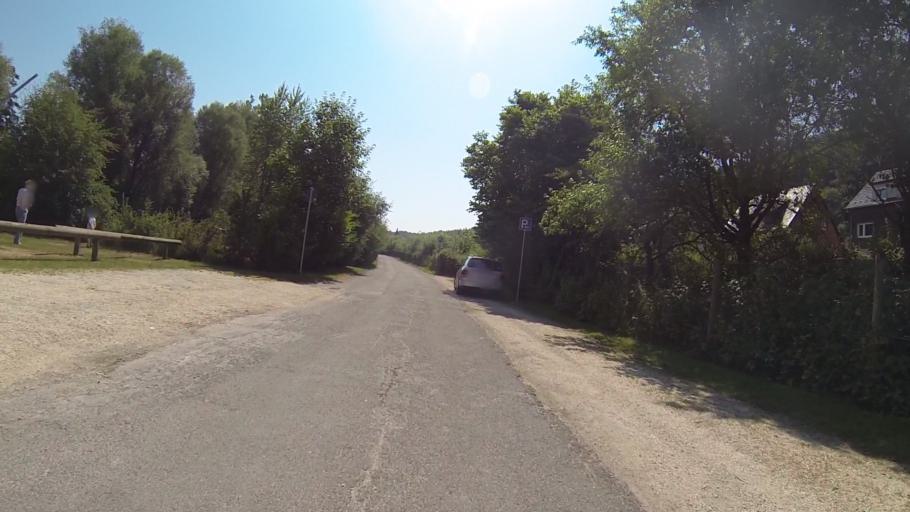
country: DE
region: Baden-Wuerttemberg
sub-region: Regierungsbezirk Stuttgart
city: Konigsbronn
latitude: 48.7318
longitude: 10.1313
